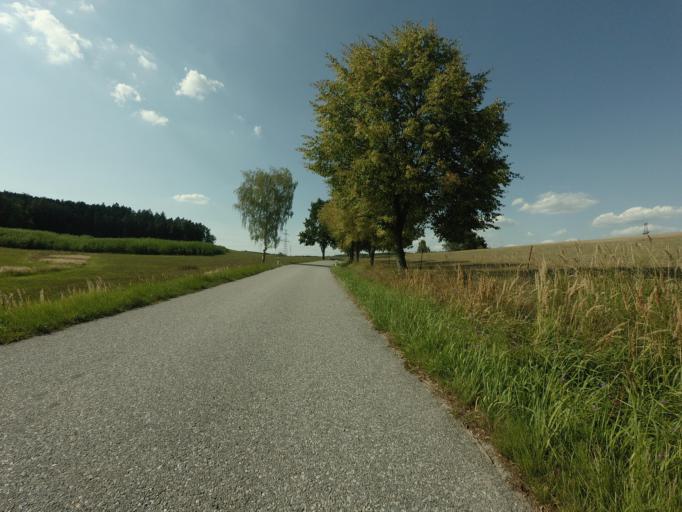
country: CZ
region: Jihocesky
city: Tyn nad Vltavou
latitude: 49.1674
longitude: 14.4255
